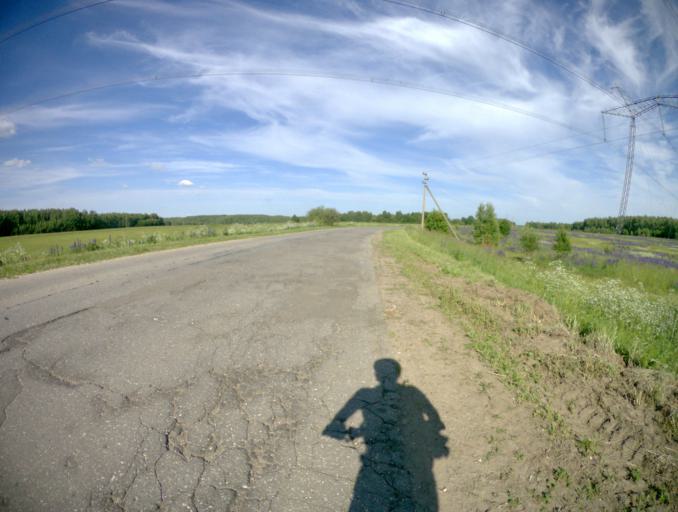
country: RU
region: Vladimir
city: Stavrovo
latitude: 56.1597
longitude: 40.0760
